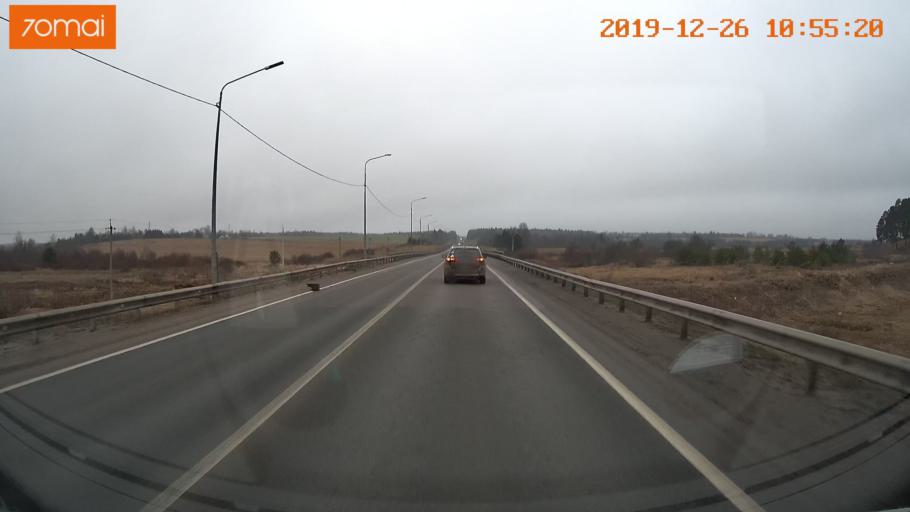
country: RU
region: Vologda
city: Molochnoye
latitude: 59.1887
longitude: 39.5845
